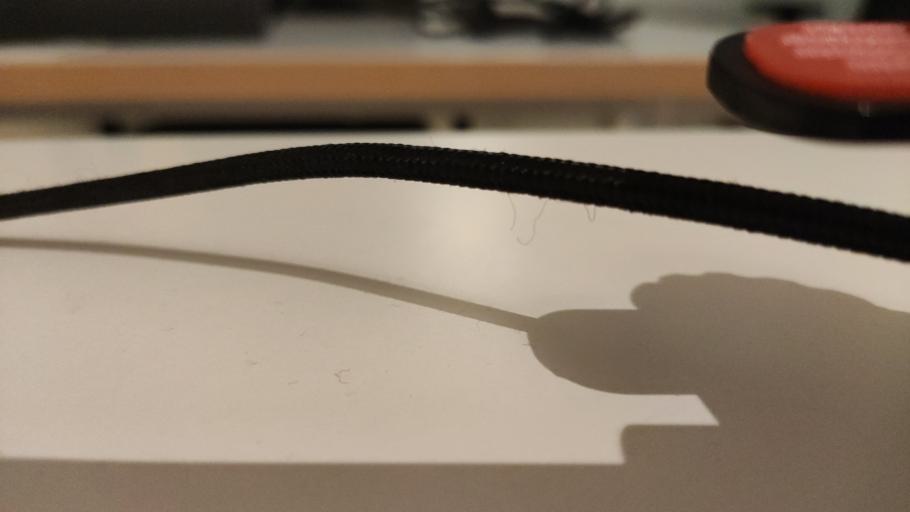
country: RU
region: Moskovskaya
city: Mikhnevo
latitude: 55.0957
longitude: 38.0101
